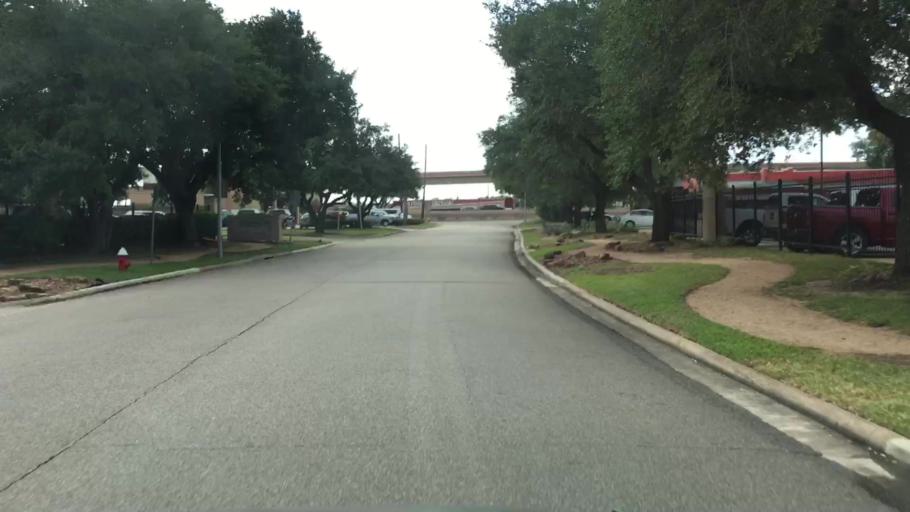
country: US
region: Texas
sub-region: Fort Bend County
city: Meadows Place
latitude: 29.6492
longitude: -95.5737
